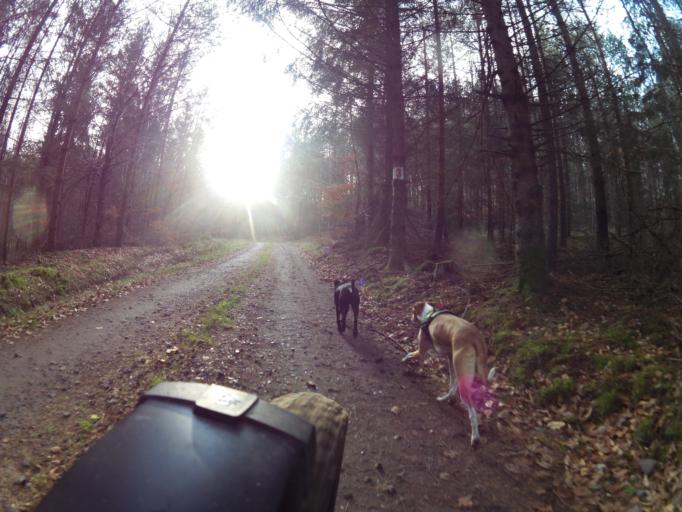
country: PL
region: West Pomeranian Voivodeship
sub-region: Powiat koszalinski
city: Polanow
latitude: 54.1833
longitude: 16.7197
